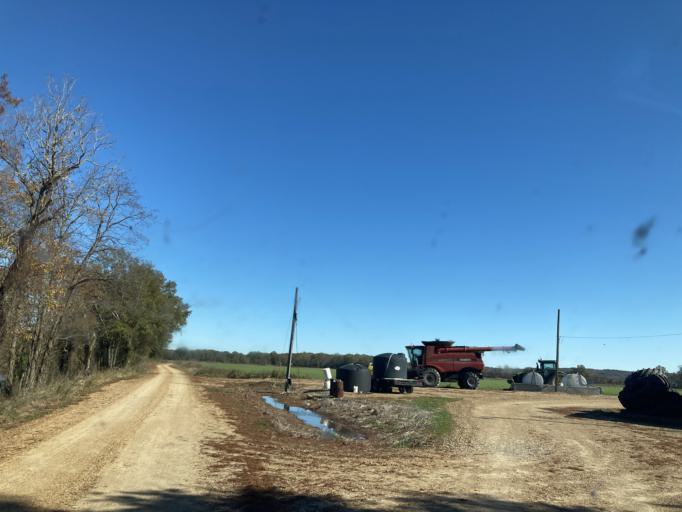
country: US
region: Mississippi
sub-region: Hinds County
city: Lynchburg
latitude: 32.6390
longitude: -90.6044
